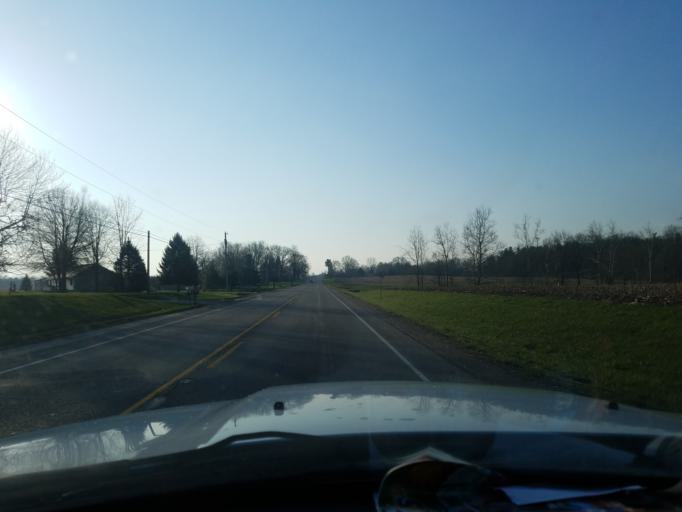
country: US
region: Indiana
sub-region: Vigo County
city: Seelyville
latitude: 39.3968
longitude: -87.3140
